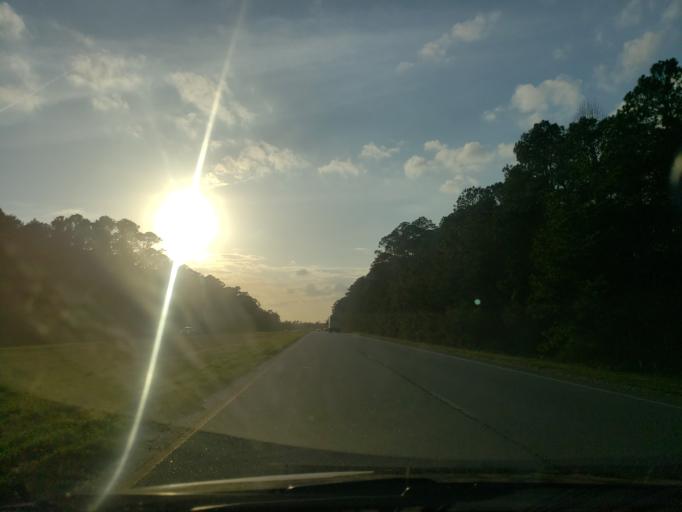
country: US
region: Georgia
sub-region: Chatham County
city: Bloomingdale
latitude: 32.1485
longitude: -81.2904
